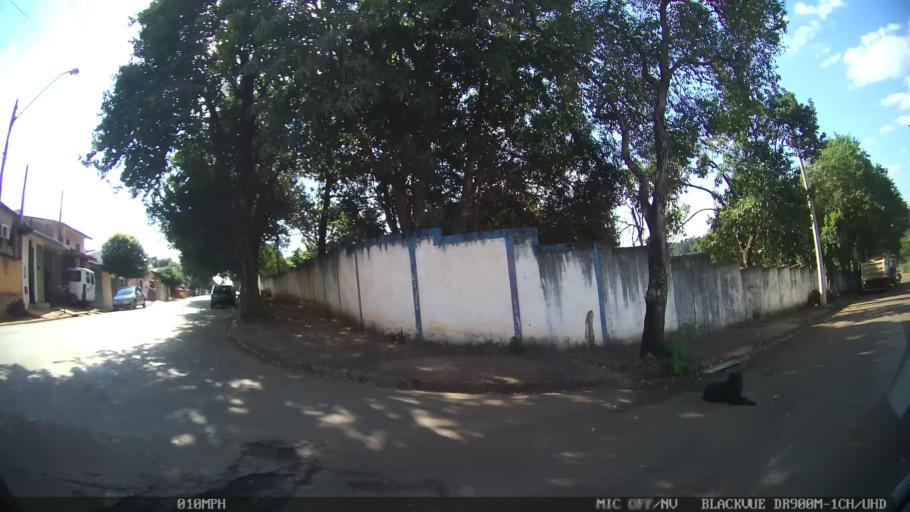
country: BR
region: Sao Paulo
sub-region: Sumare
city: Sumare
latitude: -22.8328
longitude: -47.2599
